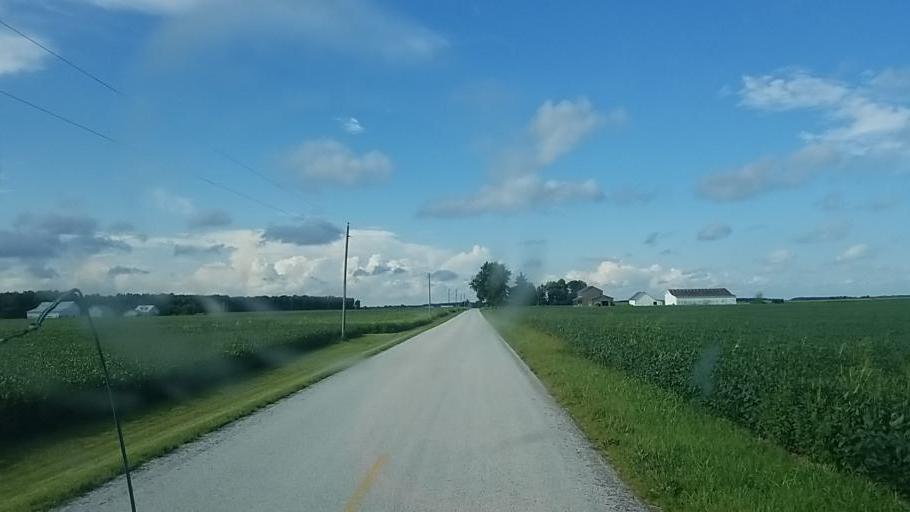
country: US
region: Ohio
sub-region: Hardin County
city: Forest
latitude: 40.7409
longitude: -83.5159
